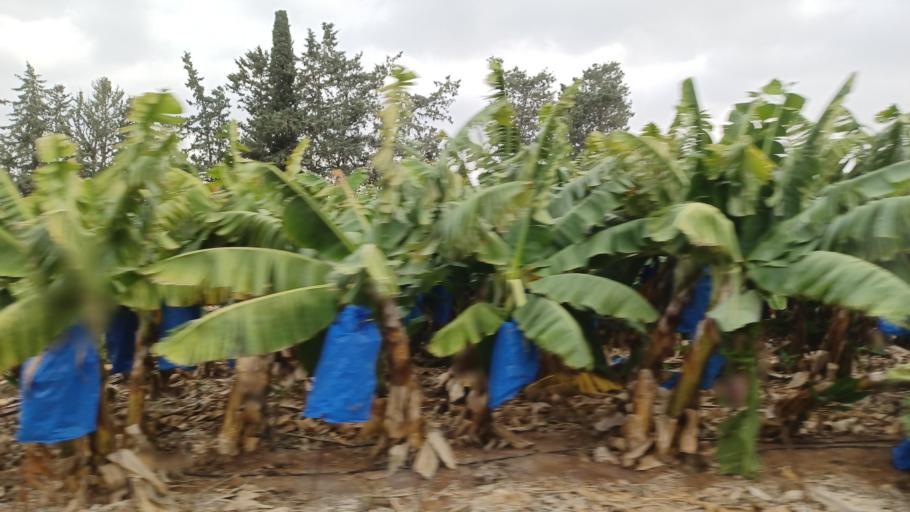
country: CY
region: Pafos
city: Pegeia
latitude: 34.8976
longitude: 32.3350
